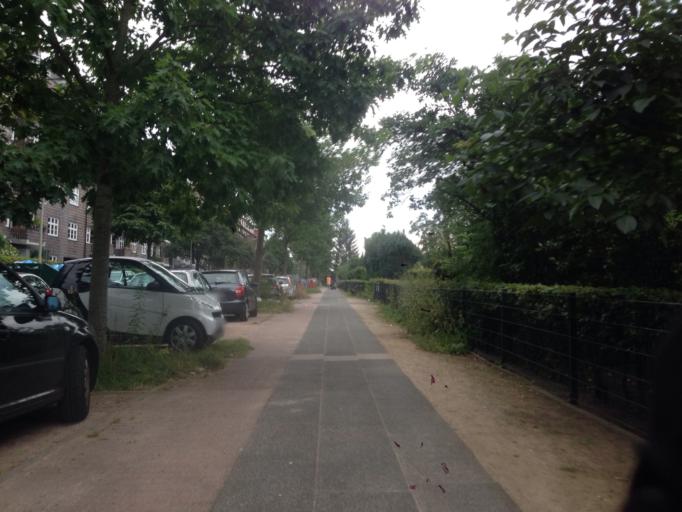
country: DE
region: Hamburg
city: Barmbek-Nord
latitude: 53.5968
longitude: 10.0370
